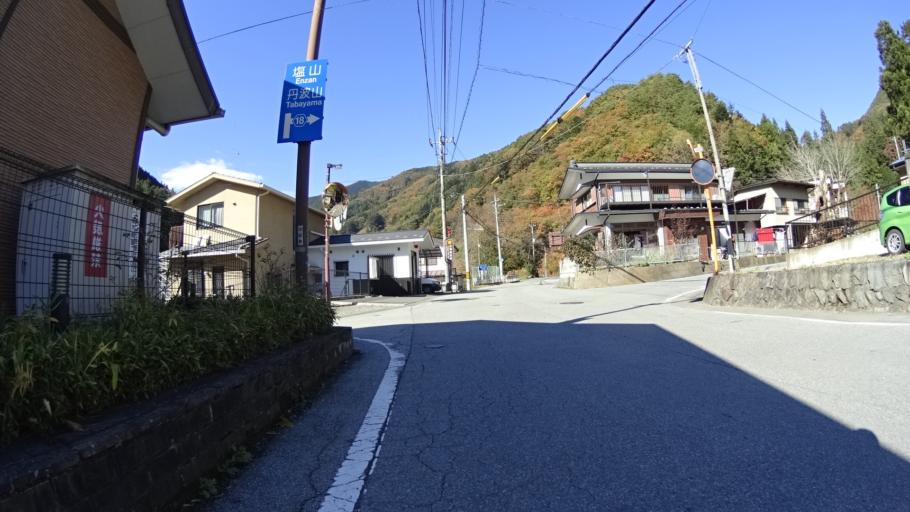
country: JP
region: Yamanashi
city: Otsuki
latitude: 35.7608
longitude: 138.9385
